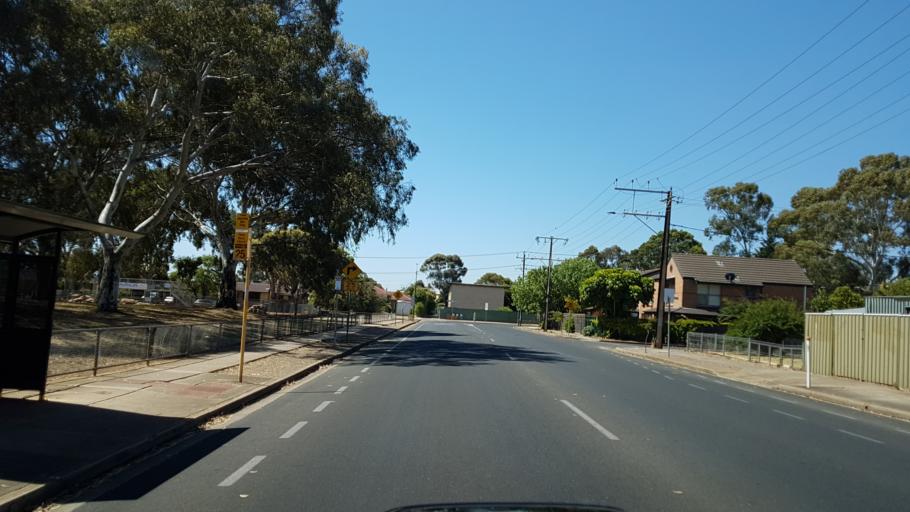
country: AU
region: South Australia
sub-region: Marion
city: Clovelly Park
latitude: -35.0011
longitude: 138.5653
